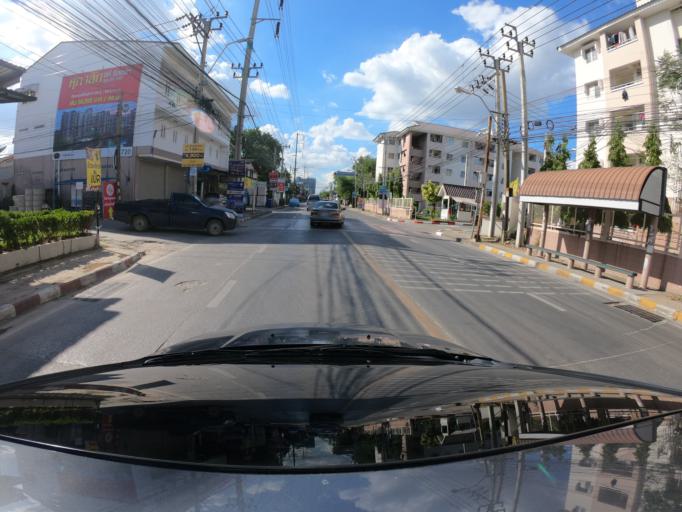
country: TH
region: Bangkok
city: Bang Na
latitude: 13.6532
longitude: 100.6149
